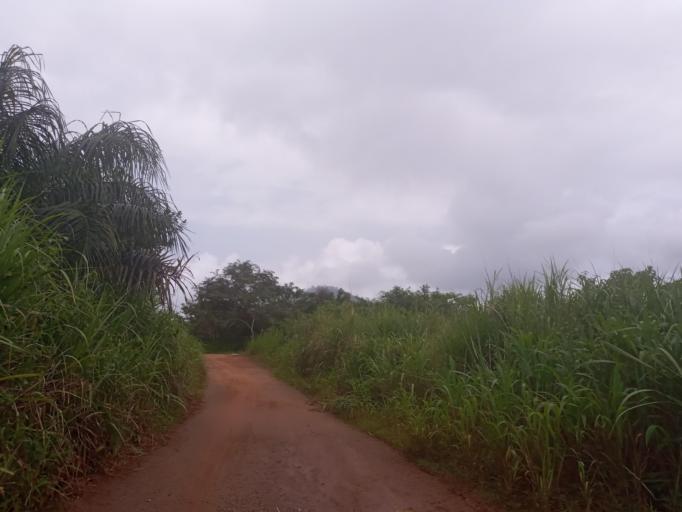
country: SL
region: Northern Province
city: Bumbuna
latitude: 8.9623
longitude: -11.7577
